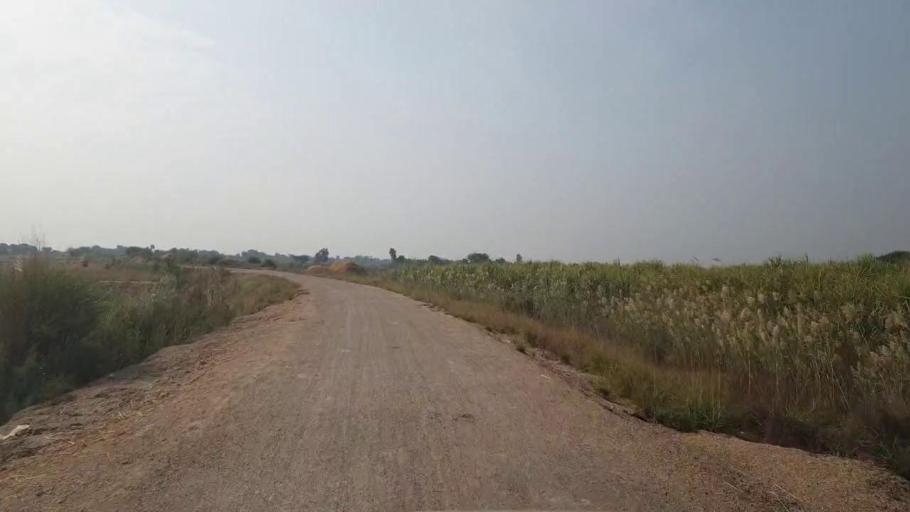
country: PK
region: Sindh
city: Tando Muhammad Khan
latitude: 25.1154
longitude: 68.4964
